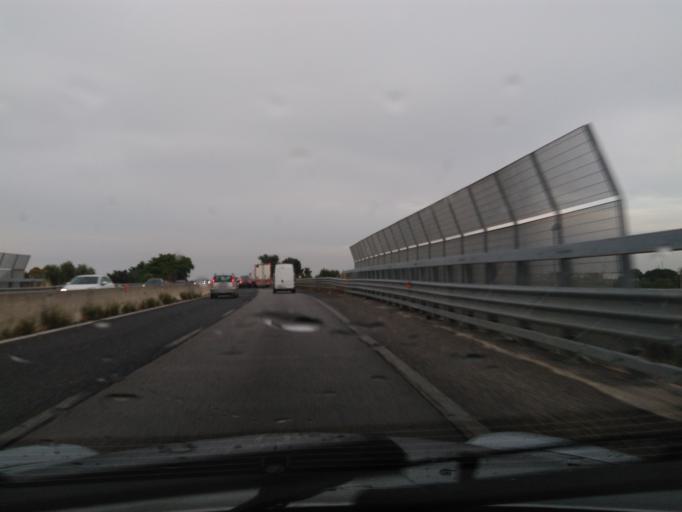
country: IT
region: Apulia
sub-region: Provincia di Bari
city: Molfetta
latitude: 41.1843
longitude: 16.5998
